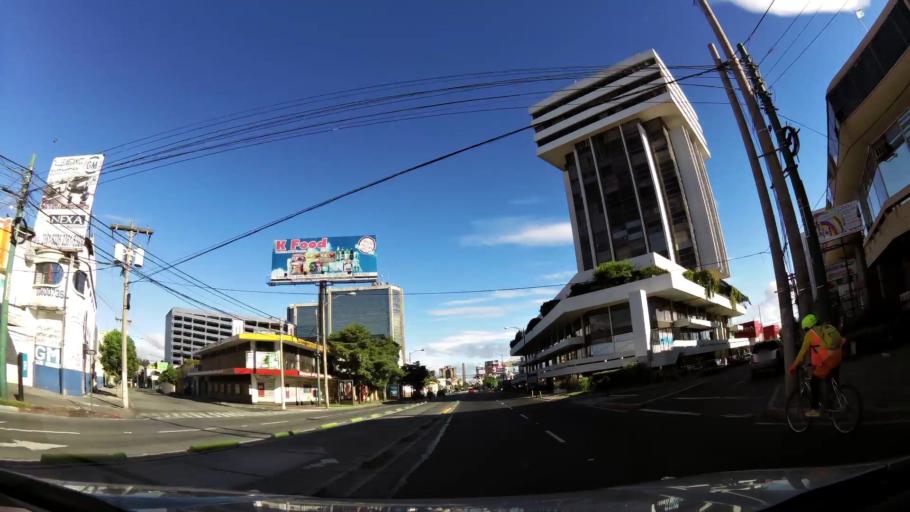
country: GT
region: Guatemala
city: Guatemala City
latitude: 14.6161
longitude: -90.5160
